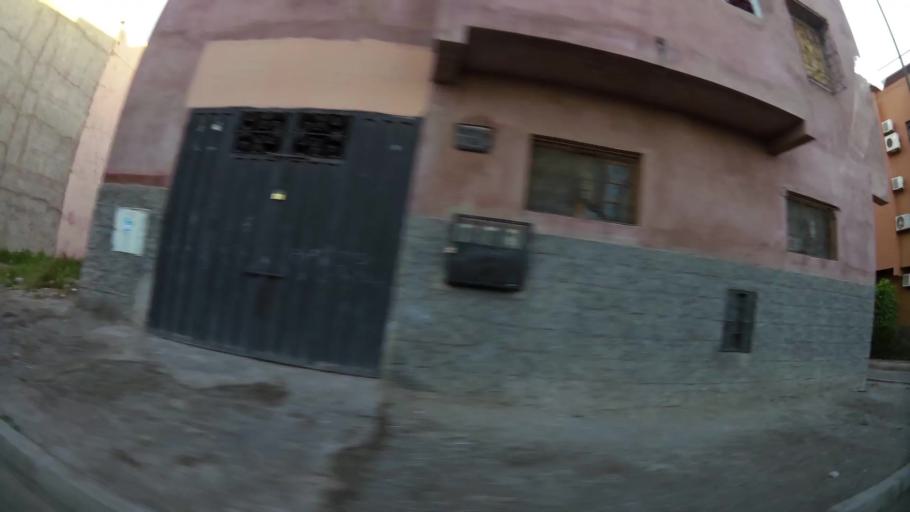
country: MA
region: Marrakech-Tensift-Al Haouz
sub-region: Marrakech
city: Marrakesh
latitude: 31.6407
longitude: -8.0393
